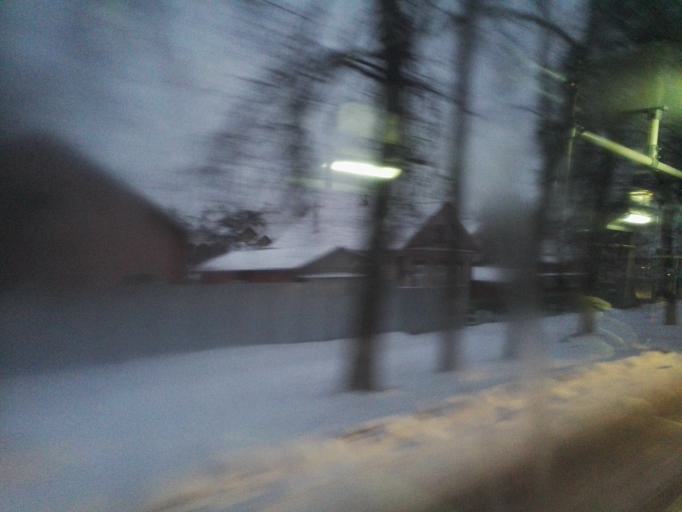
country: RU
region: Tula
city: Tula
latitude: 54.1682
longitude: 37.6024
